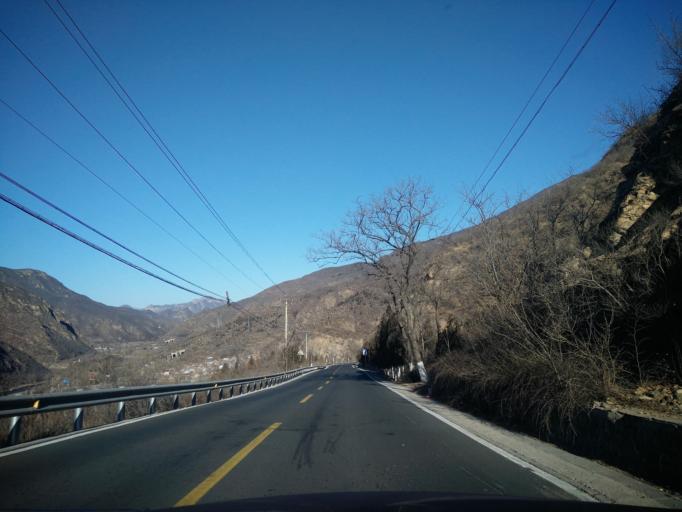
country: CN
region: Beijing
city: Wangping
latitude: 40.0033
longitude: 115.9431
